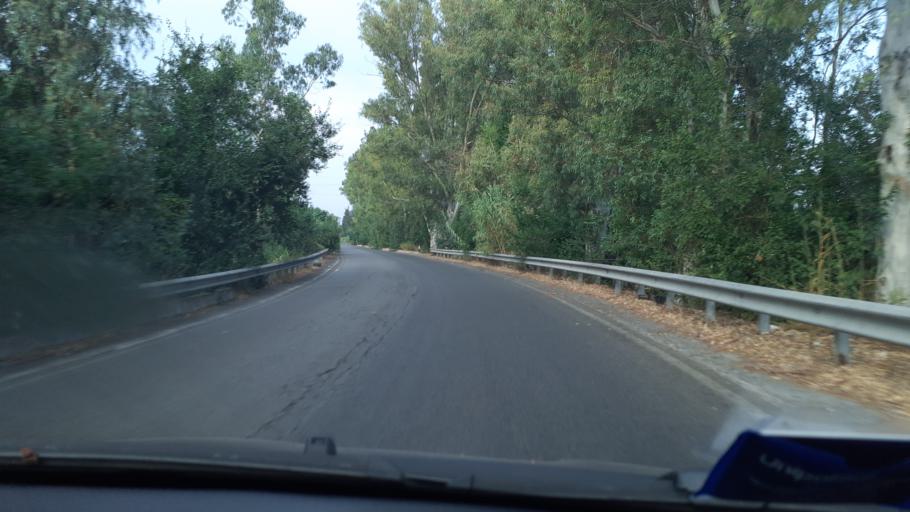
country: IT
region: Sicily
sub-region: Catania
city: Catania
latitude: 37.4507
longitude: 15.0241
